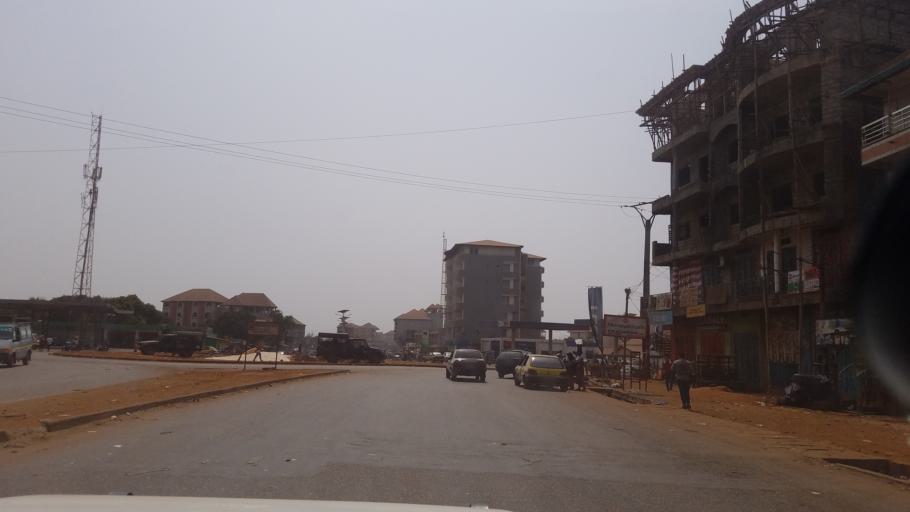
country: GN
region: Kindia
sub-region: Prefecture de Dubreka
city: Dubreka
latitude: 9.6698
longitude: -13.5577
